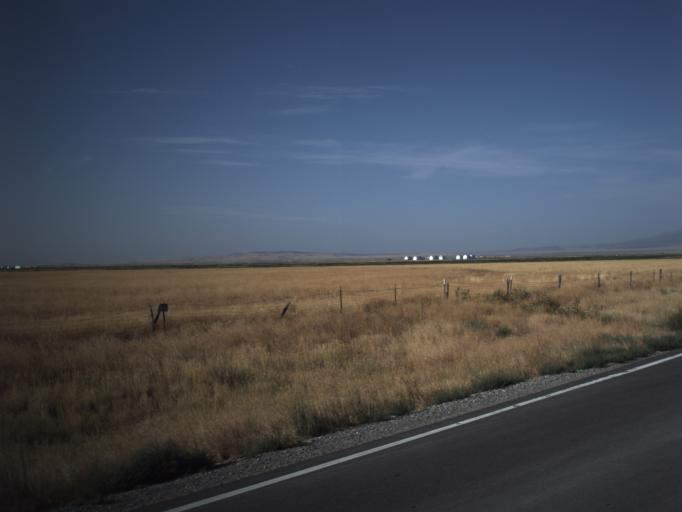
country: US
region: Idaho
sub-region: Oneida County
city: Malad City
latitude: 41.9672
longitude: -112.8431
